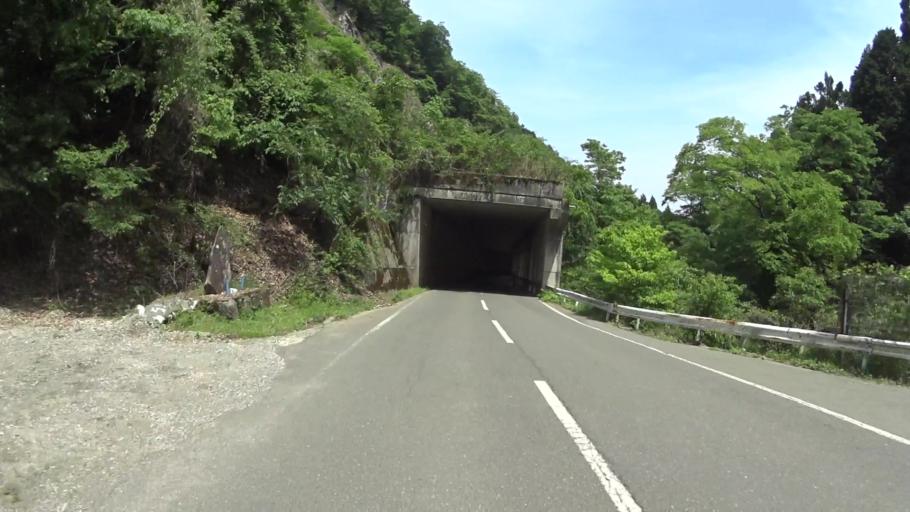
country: JP
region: Kyoto
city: Maizuru
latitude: 35.4420
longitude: 135.4957
